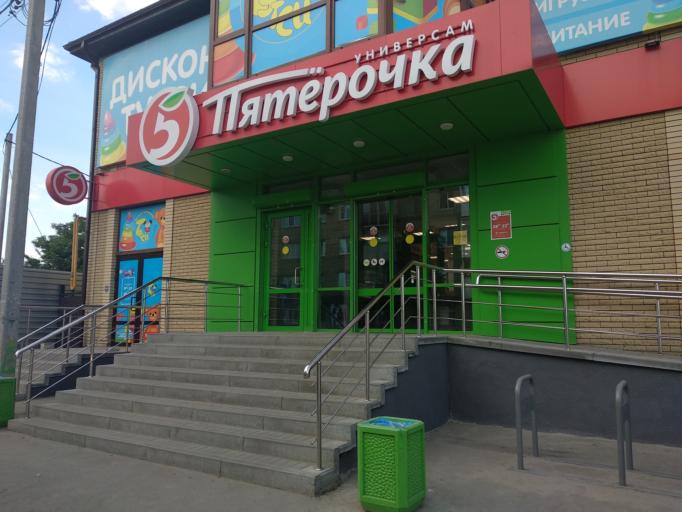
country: RU
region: Rostov
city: Millerovo
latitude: 48.9157
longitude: 40.4060
